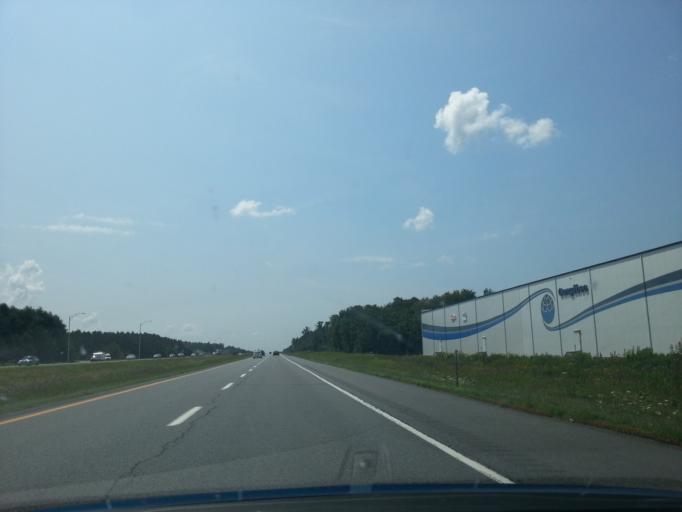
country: CA
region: Quebec
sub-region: Mauricie
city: Princeville
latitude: 46.3161
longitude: -71.9414
